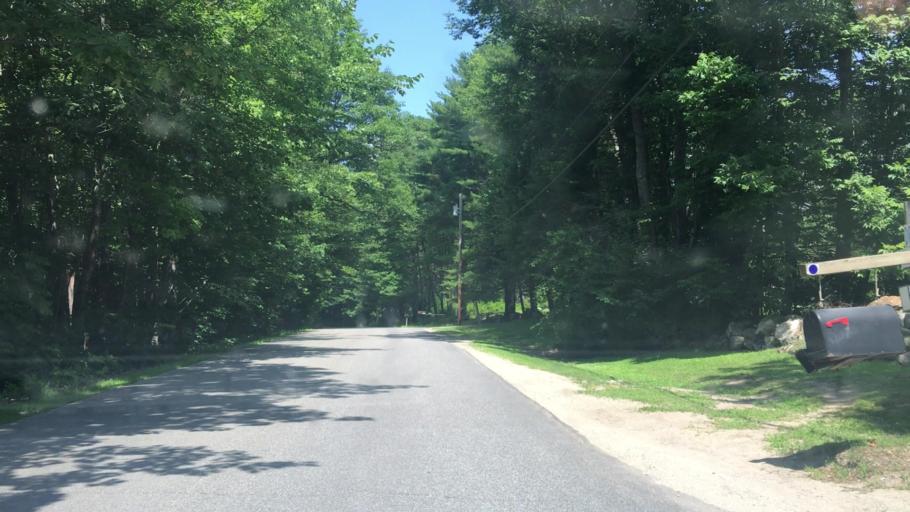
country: US
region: Maine
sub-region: Kennebec County
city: Monmouth
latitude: 44.2782
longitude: -70.0512
